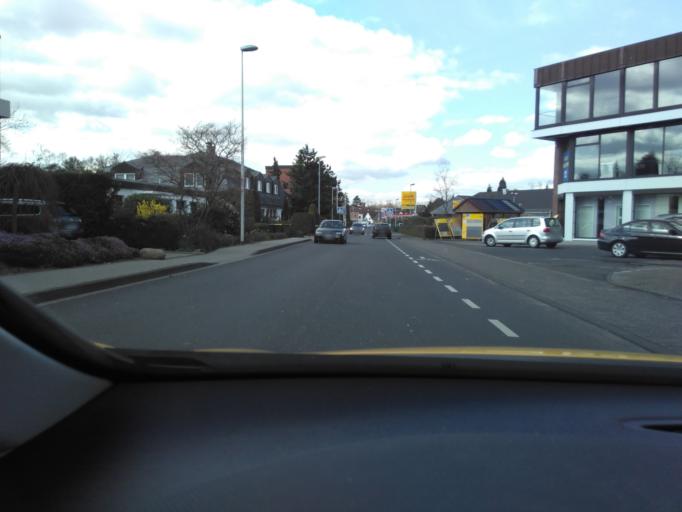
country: DE
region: North Rhine-Westphalia
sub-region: Regierungsbezirk Koln
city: Erftstadt
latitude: 50.7978
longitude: 6.7769
